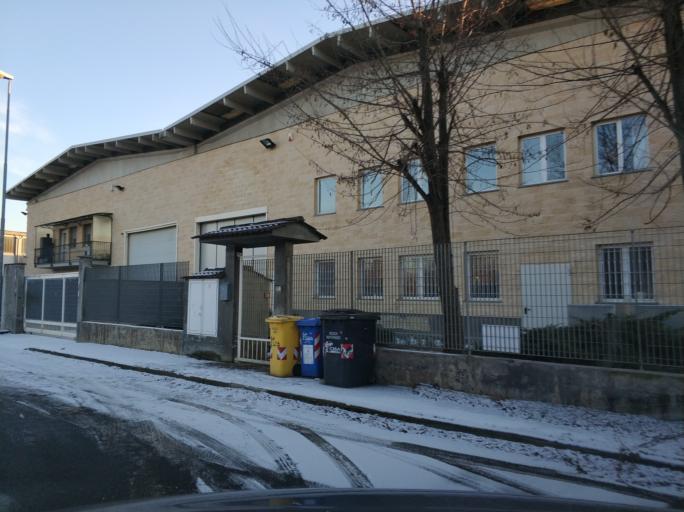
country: IT
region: Piedmont
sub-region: Provincia di Torino
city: Grosso
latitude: 45.2630
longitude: 7.5702
